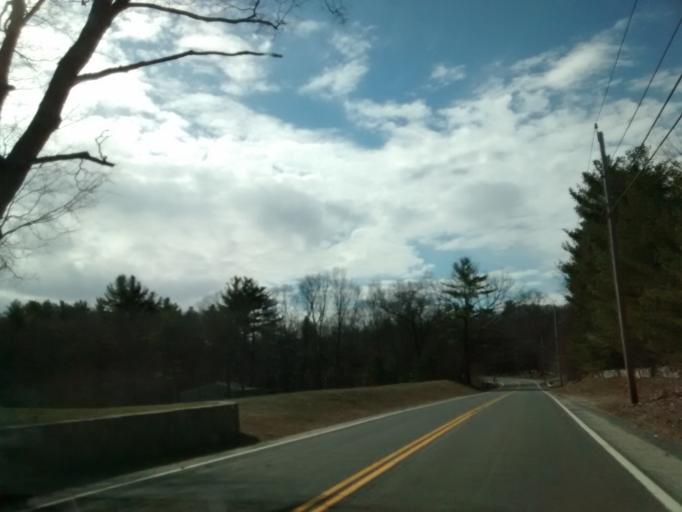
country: US
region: Rhode Island
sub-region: Providence County
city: Harrisville
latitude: 41.9841
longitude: -71.6956
